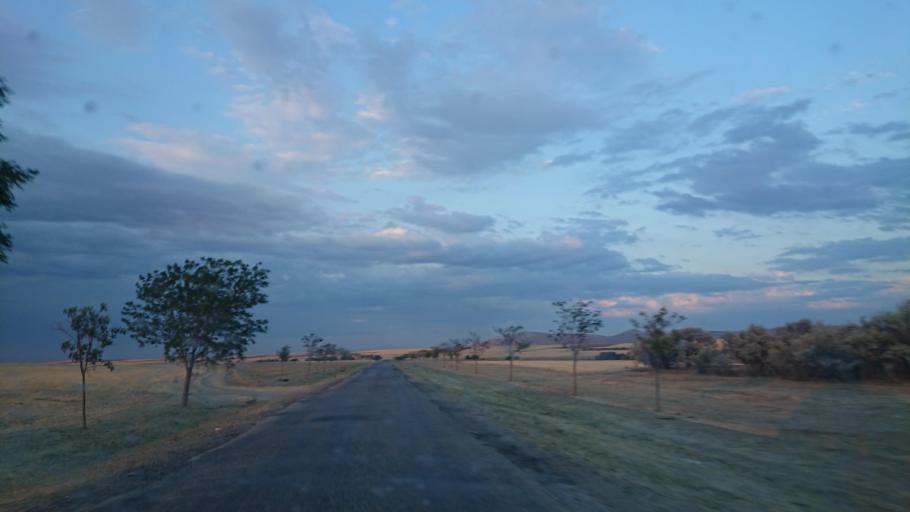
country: TR
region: Aksaray
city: Balci
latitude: 38.8257
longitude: 34.1179
